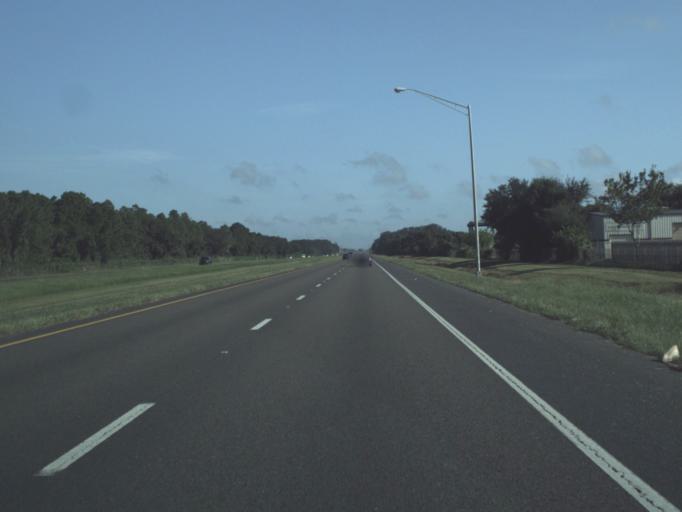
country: US
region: Florida
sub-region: Manatee County
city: Samoset
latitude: 27.4311
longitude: -82.5303
